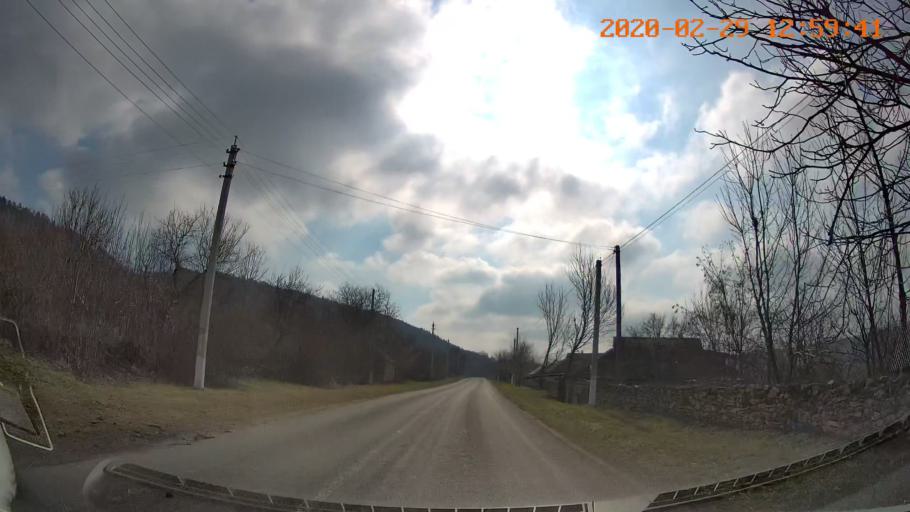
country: MD
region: Telenesti
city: Camenca
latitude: 48.0597
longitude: 28.7251
